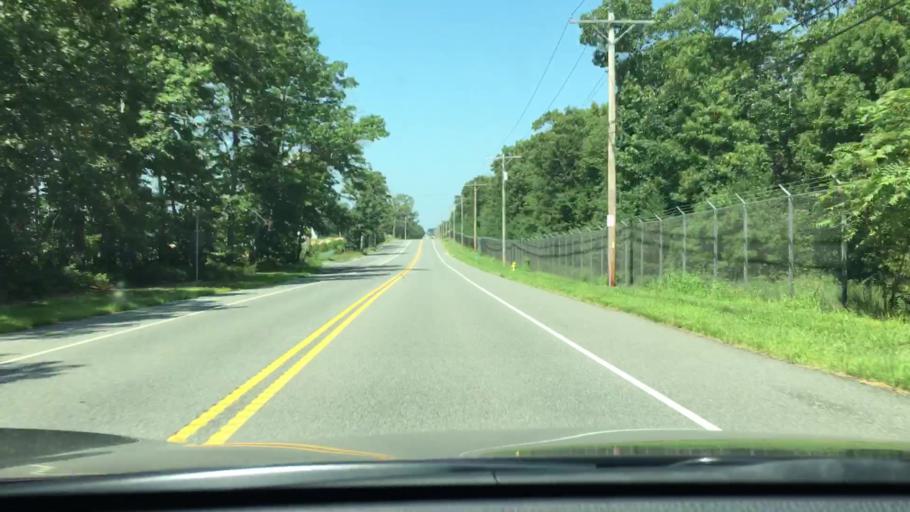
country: US
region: New Jersey
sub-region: Cumberland County
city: Laurel Lake
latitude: 39.3581
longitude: -75.0700
